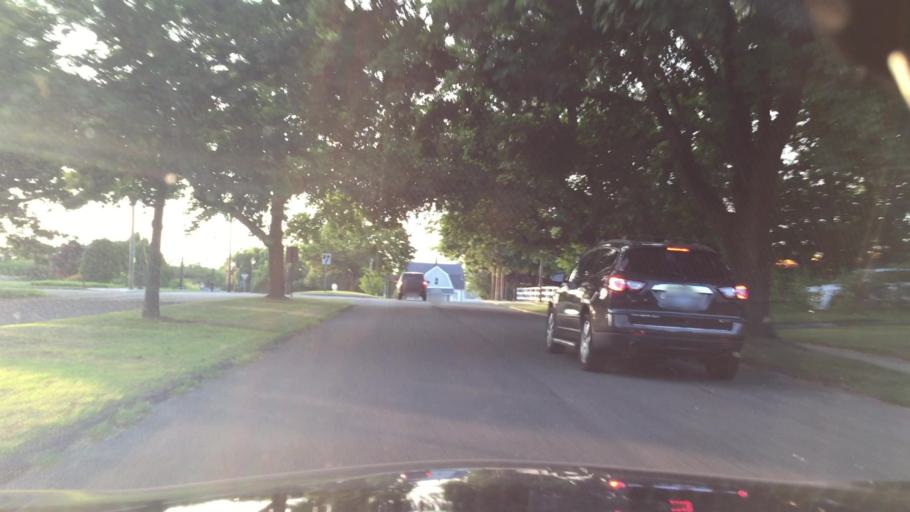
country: US
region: Connecticut
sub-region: Fairfield County
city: Stratford
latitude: 41.1989
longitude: -73.1079
